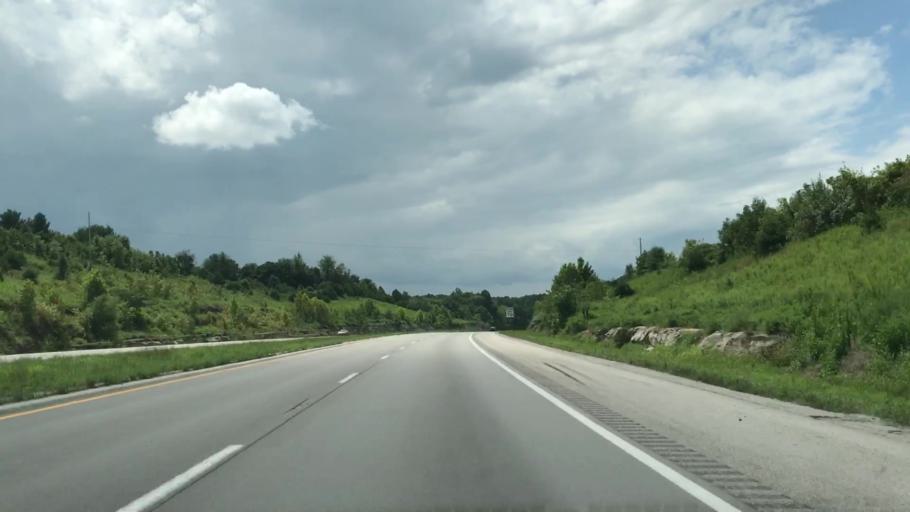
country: US
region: Kentucky
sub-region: Pulaski County
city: Somerset
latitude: 37.1016
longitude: -84.6678
